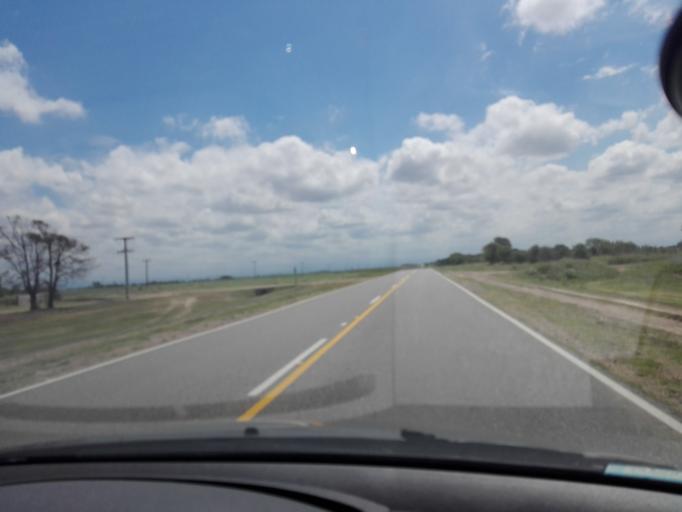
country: AR
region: Cordoba
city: Toledo
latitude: -31.6484
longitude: -64.1063
